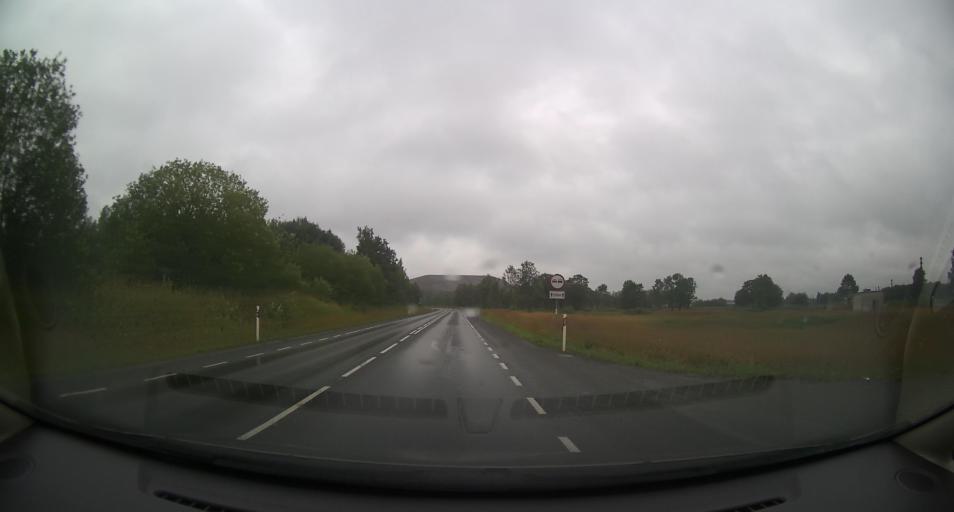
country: EE
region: Ida-Virumaa
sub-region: Kivioli linn
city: Kivioli
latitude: 59.3588
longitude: 26.9485
